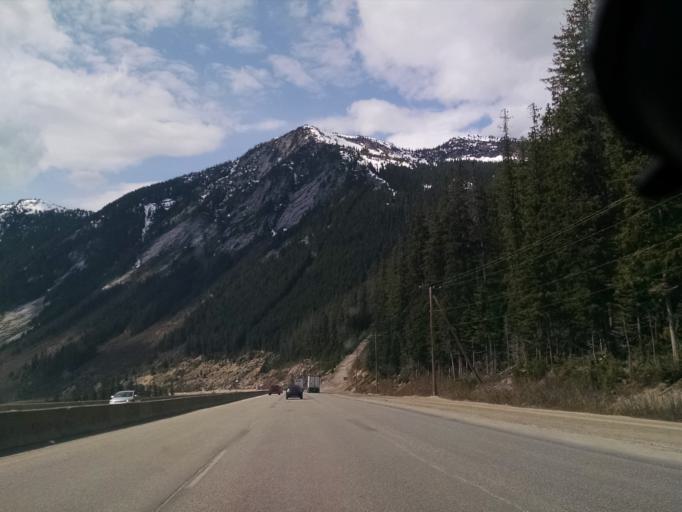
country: CA
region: British Columbia
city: Hope
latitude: 49.5981
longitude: -121.1470
